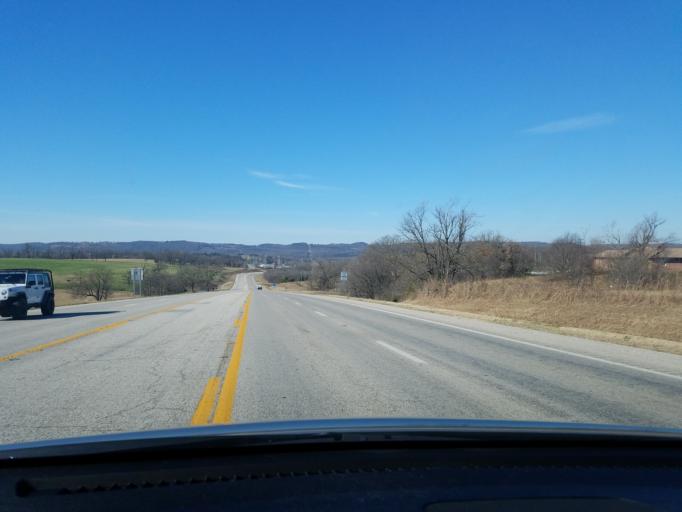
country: US
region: Arkansas
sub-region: Carroll County
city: Berryville
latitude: 36.3902
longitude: -93.6225
